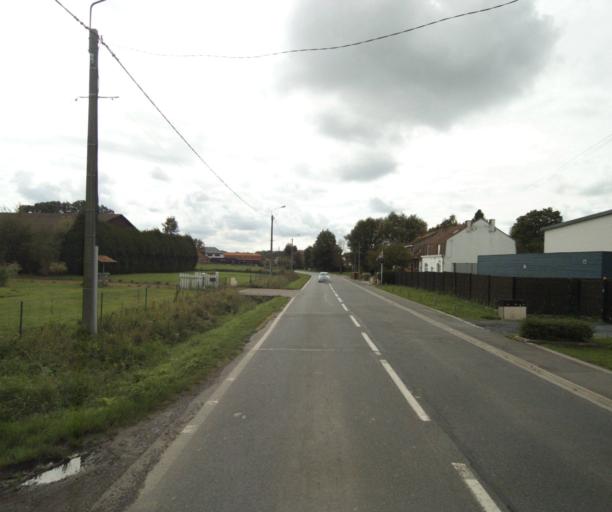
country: FR
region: Nord-Pas-de-Calais
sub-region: Departement du Nord
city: Premesques
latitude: 50.6565
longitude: 2.9567
